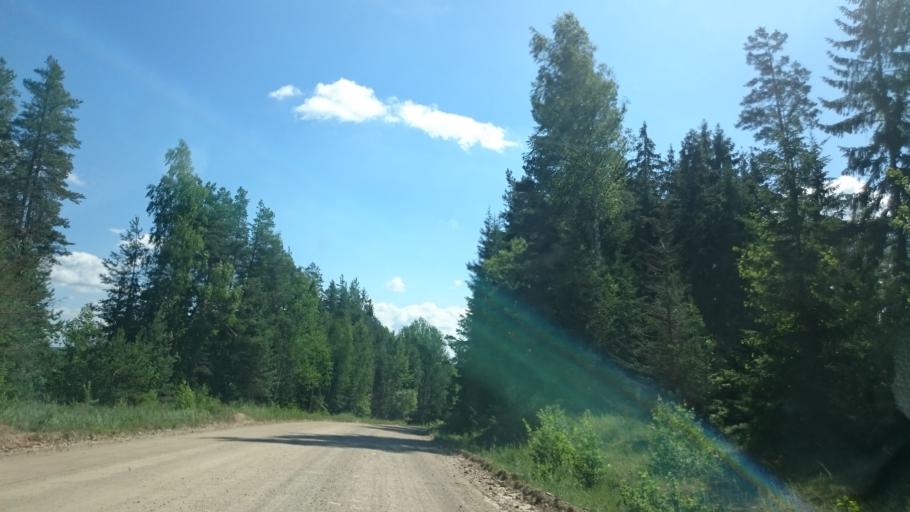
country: LV
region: Cibla
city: Cibla
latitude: 56.5406
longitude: 27.9422
